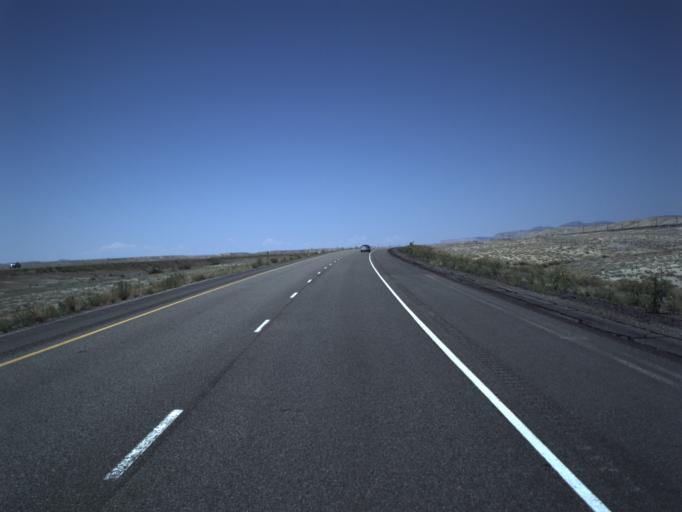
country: US
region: Utah
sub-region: Grand County
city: Moab
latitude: 38.9331
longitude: -109.4330
